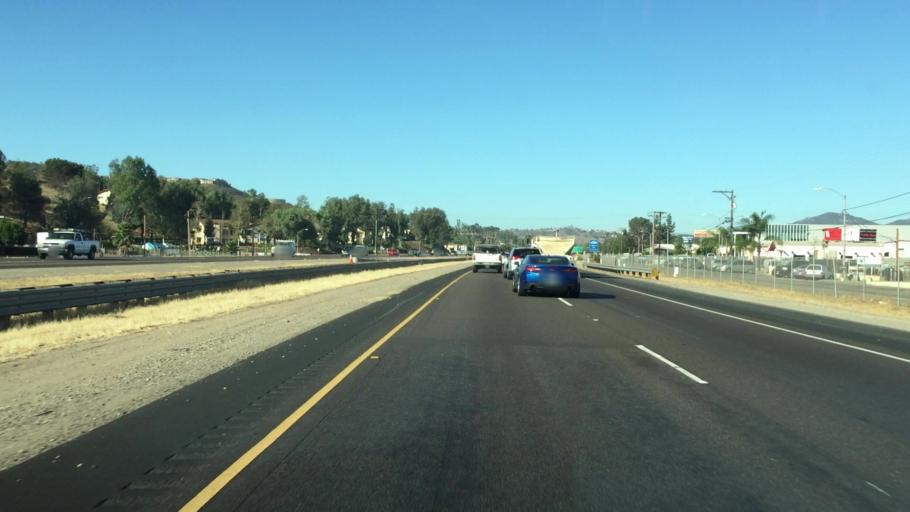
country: US
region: California
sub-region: San Diego County
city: Santee
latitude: 32.8509
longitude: -116.9519
